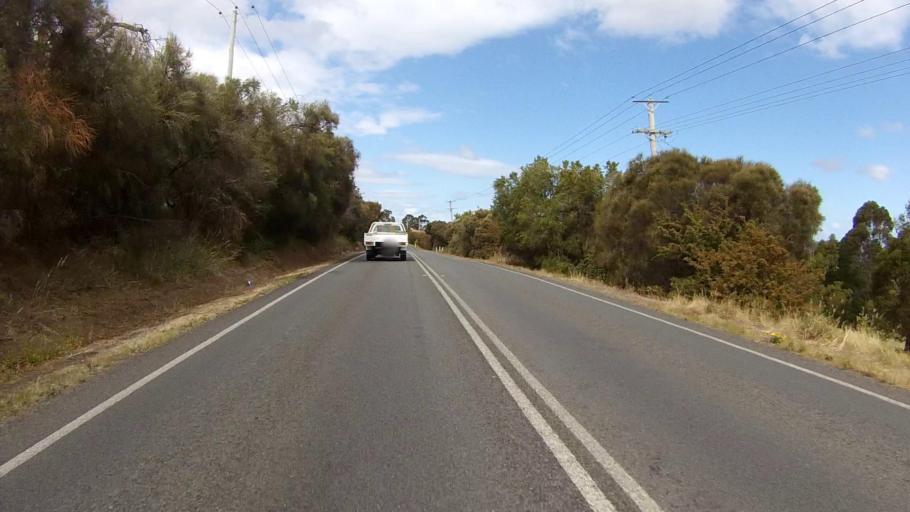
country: AU
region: Tasmania
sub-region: Clarence
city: Rokeby
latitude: -42.9068
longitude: 147.4639
